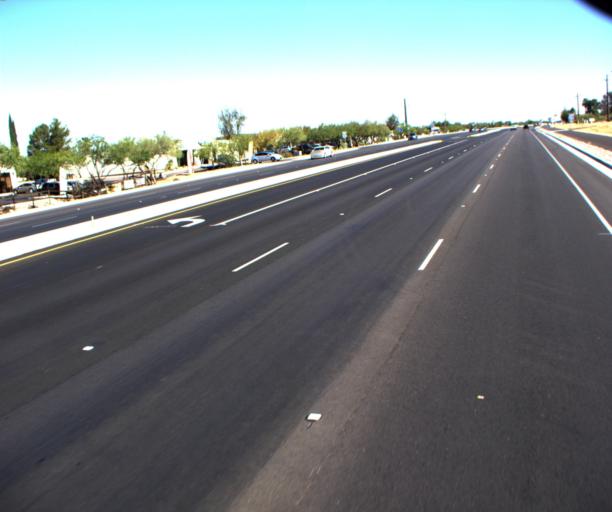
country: US
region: Arizona
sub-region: Pima County
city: Catalina
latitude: 32.4890
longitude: -110.9239
